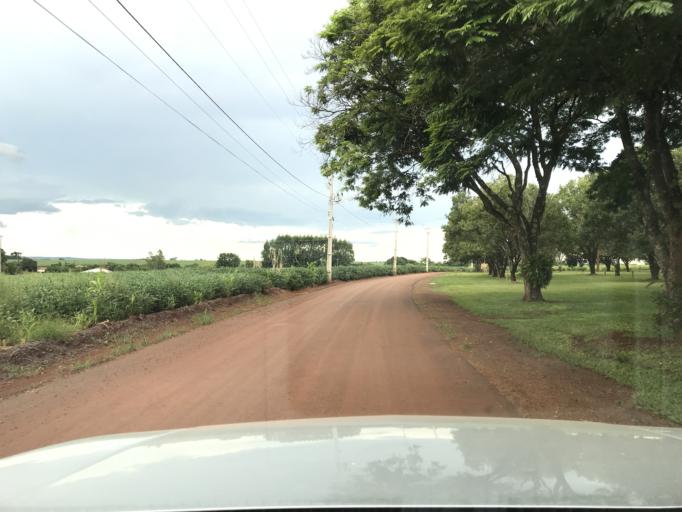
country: BR
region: Parana
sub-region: Palotina
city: Palotina
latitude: -24.2765
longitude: -53.7915
